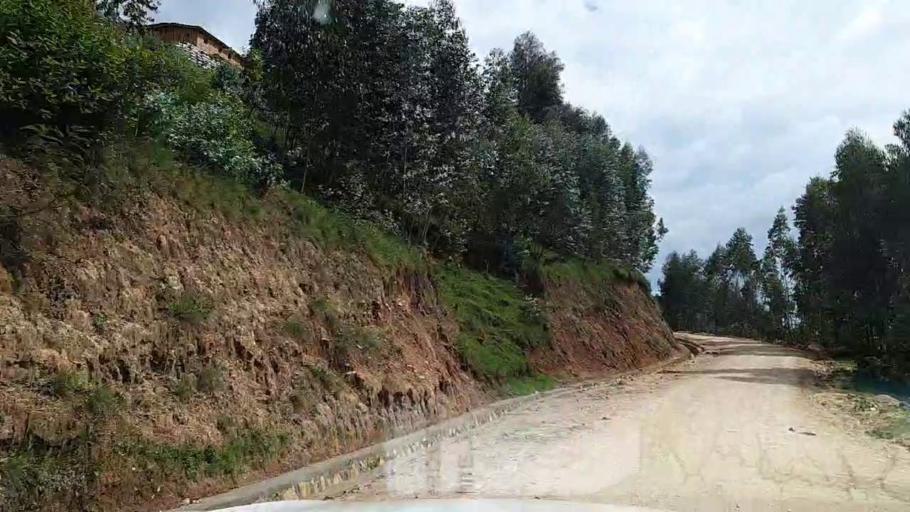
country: RW
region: Southern Province
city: Nzega
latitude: -2.3339
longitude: 29.4434
